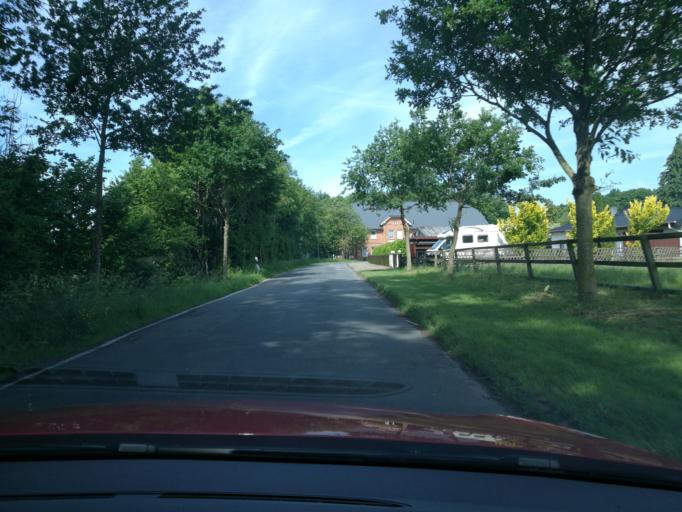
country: DE
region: Schleswig-Holstein
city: Lasbek
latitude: 53.7434
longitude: 10.3455
